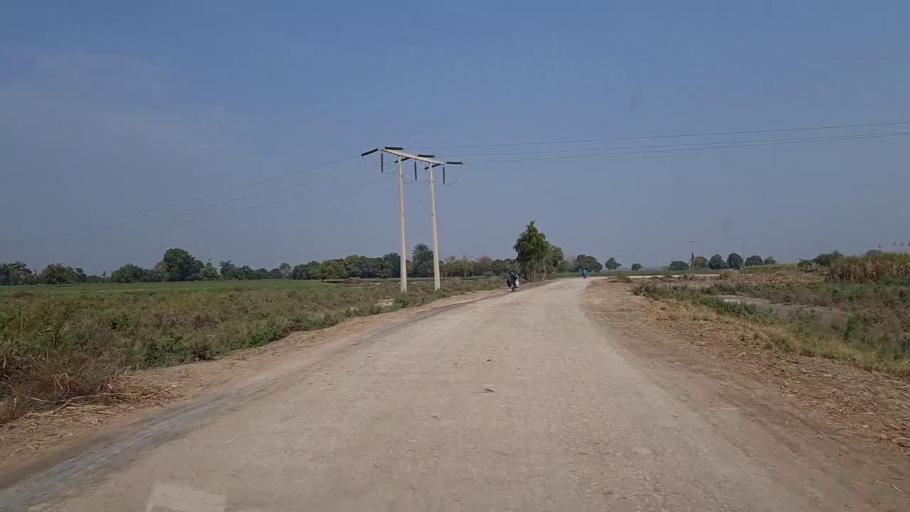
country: PK
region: Sindh
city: Mirwah Gorchani
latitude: 25.3142
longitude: 69.0583
